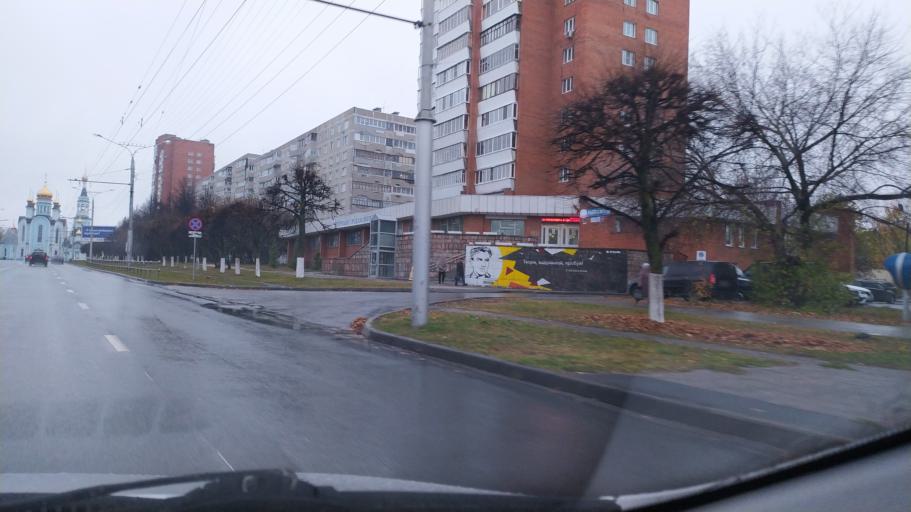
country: RU
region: Chuvashia
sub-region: Cheboksarskiy Rayon
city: Cheboksary
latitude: 56.1441
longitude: 47.1859
